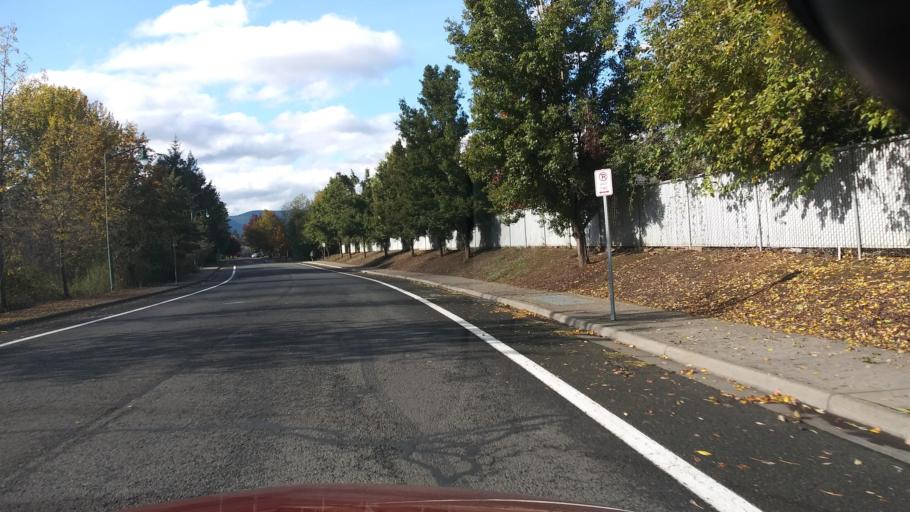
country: US
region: Oregon
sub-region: Washington County
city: Forest Grove
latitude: 45.5338
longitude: -123.1134
